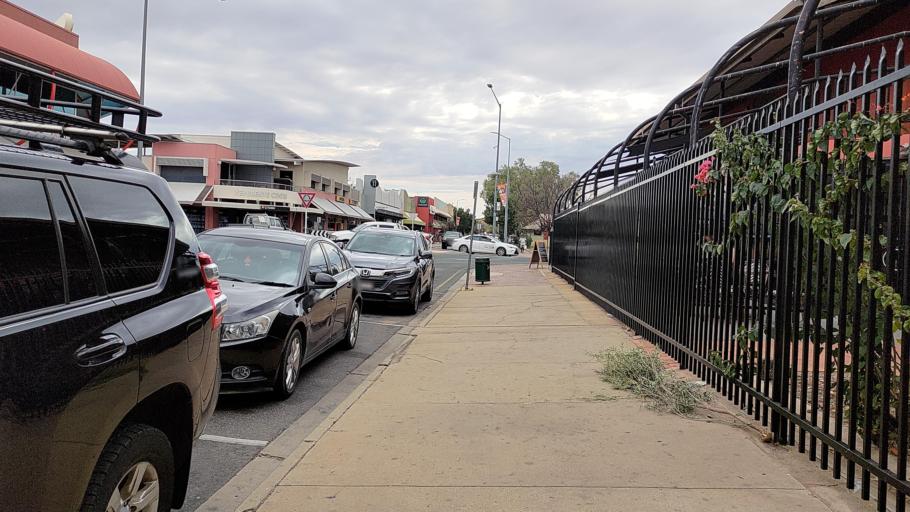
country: AU
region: Northern Territory
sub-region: Alice Springs
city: Alice Springs
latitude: -23.7007
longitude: 133.8807
